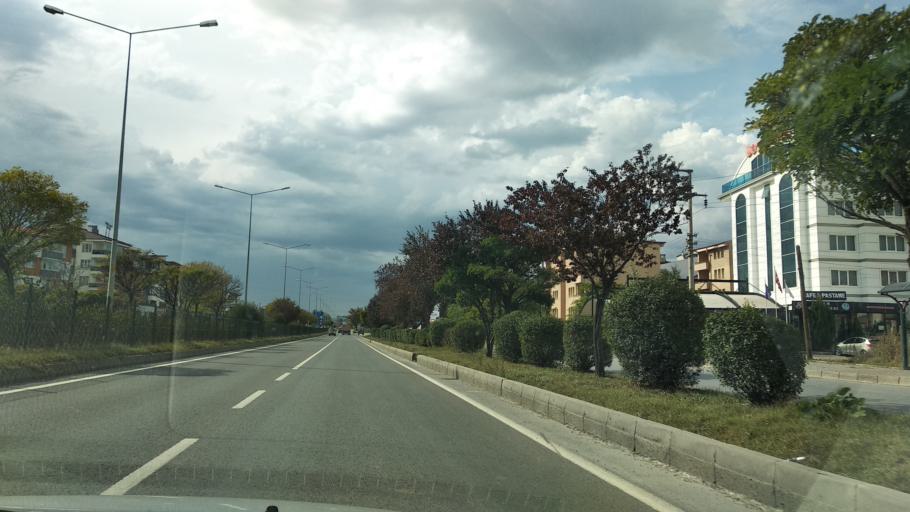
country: TR
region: Bolu
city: Bolu
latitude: 40.7364
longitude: 31.5916
